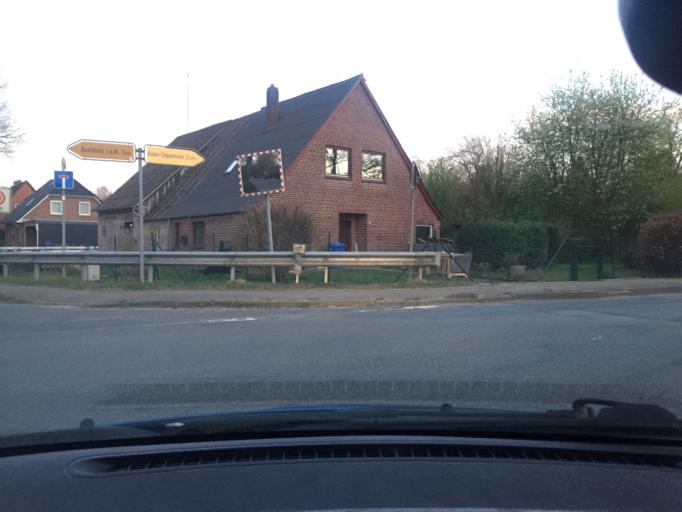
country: DE
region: Lower Saxony
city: Buchholz in der Nordheide
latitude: 53.3014
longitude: 9.8760
